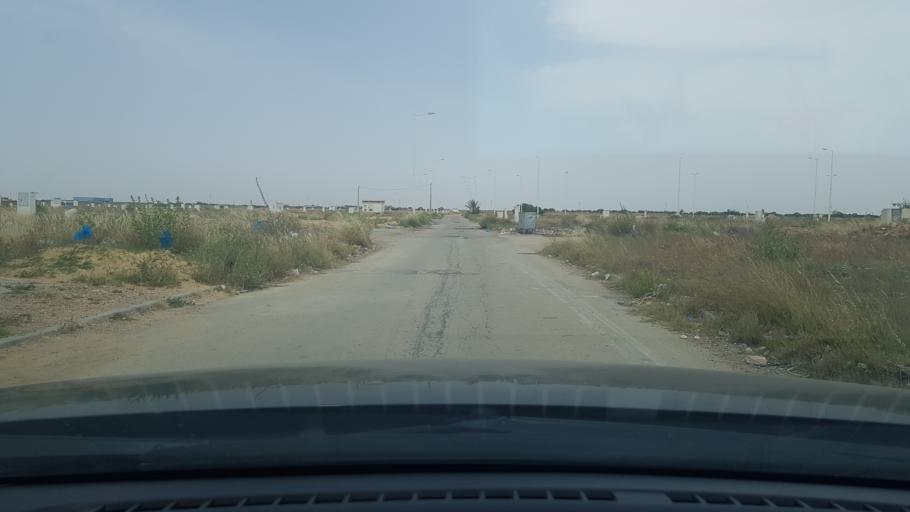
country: TN
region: Safaqis
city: Al Qarmadah
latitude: 34.8262
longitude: 10.7466
